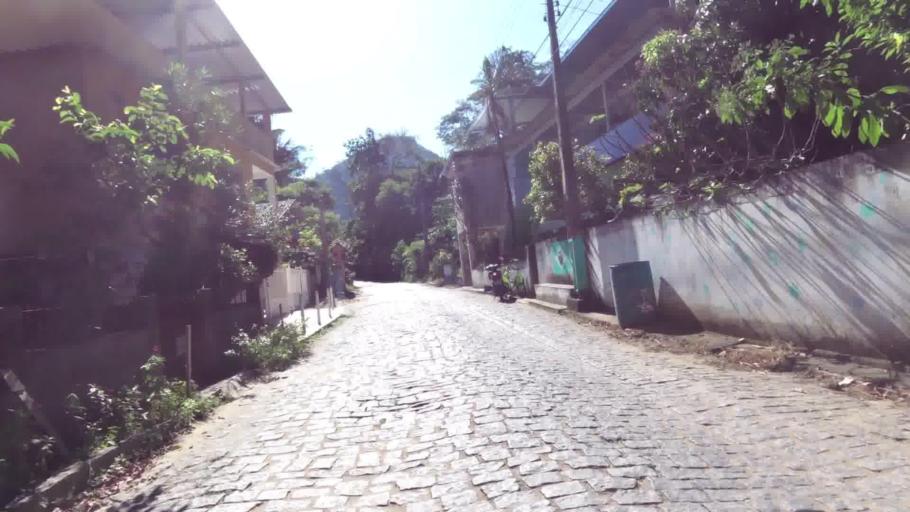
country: BR
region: Espirito Santo
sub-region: Rio Novo Do Sul
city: Rio Novo do Sul
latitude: -20.8548
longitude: -40.9252
